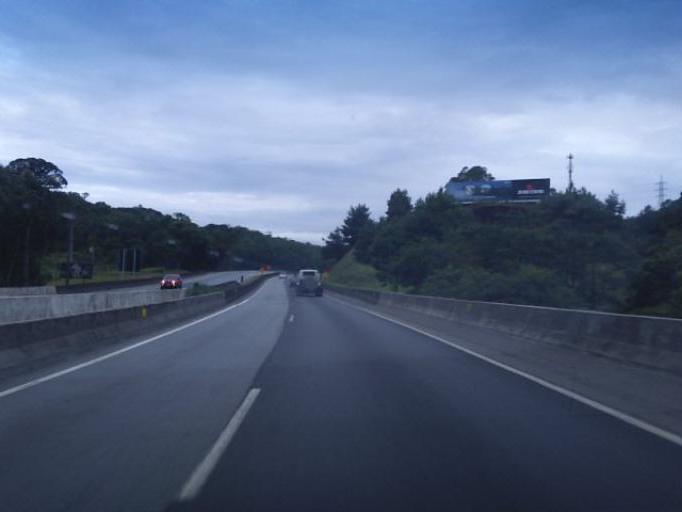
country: BR
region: Parana
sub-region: Guaratuba
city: Guaratuba
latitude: -25.8525
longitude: -48.9726
